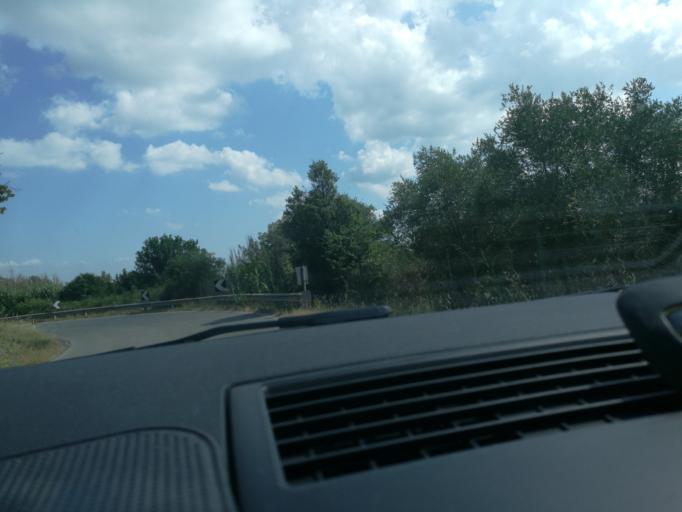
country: IT
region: Umbria
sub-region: Provincia di Terni
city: Amelia
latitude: 42.5601
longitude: 12.4398
